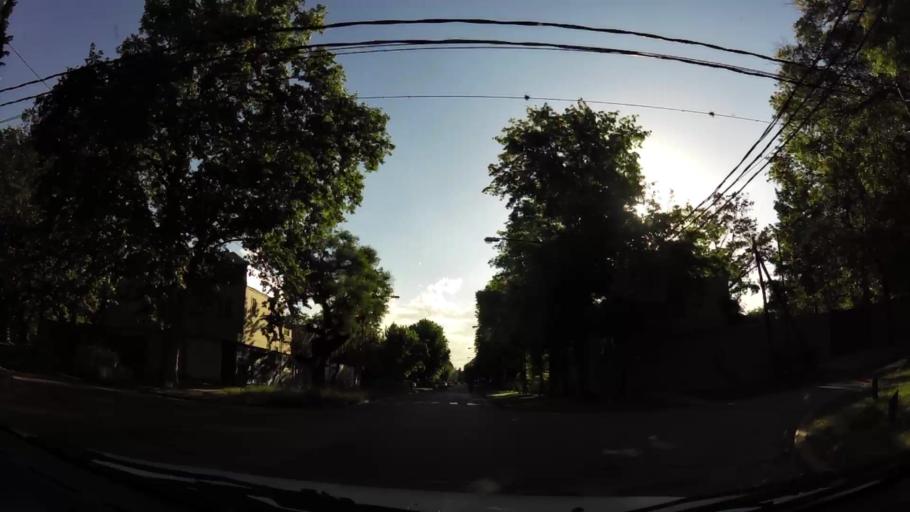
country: AR
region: Buenos Aires
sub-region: Partido de San Isidro
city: San Isidro
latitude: -34.4848
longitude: -58.5439
